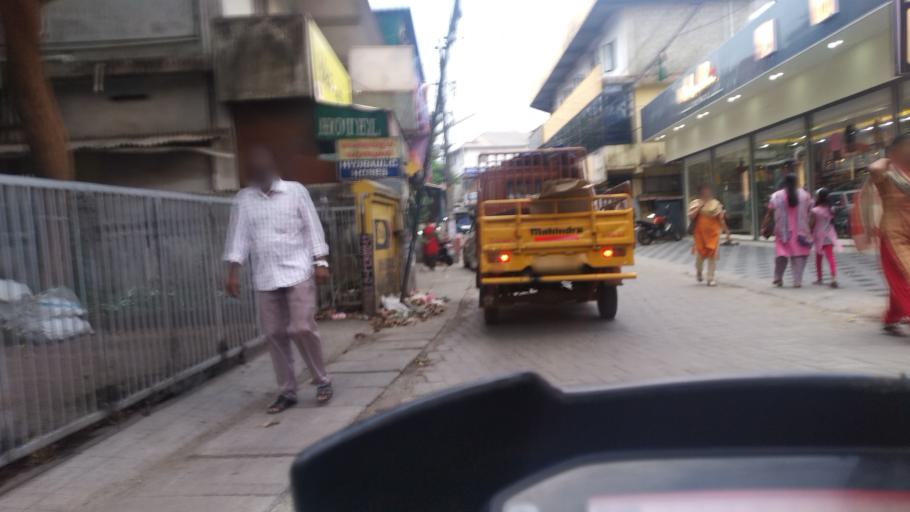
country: IN
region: Kerala
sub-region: Ernakulam
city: Elur
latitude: 10.0129
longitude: 76.3263
